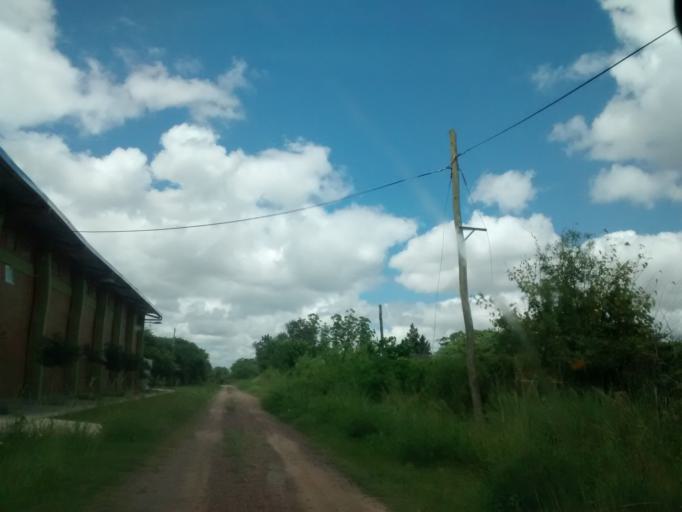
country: AR
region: Chaco
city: Fontana
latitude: -27.4103
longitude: -58.9806
